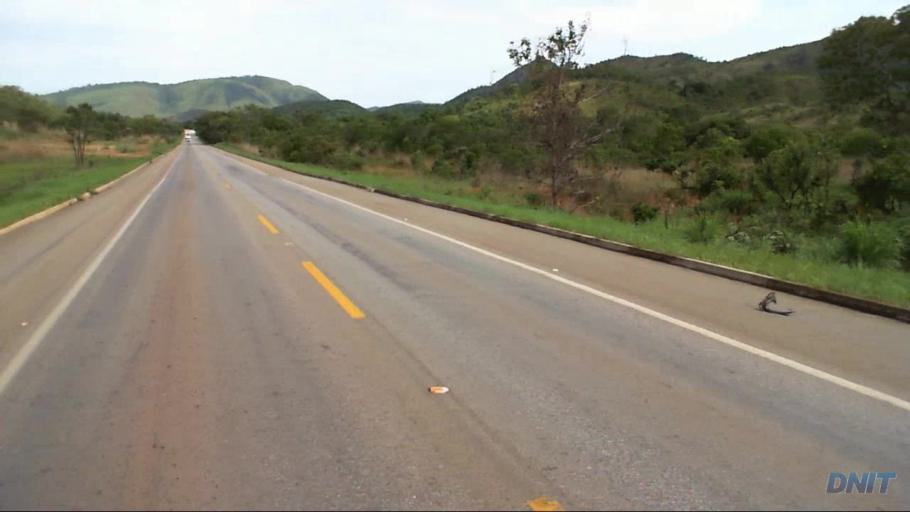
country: BR
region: Goias
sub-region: Barro Alto
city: Barro Alto
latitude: -15.1672
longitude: -48.7978
